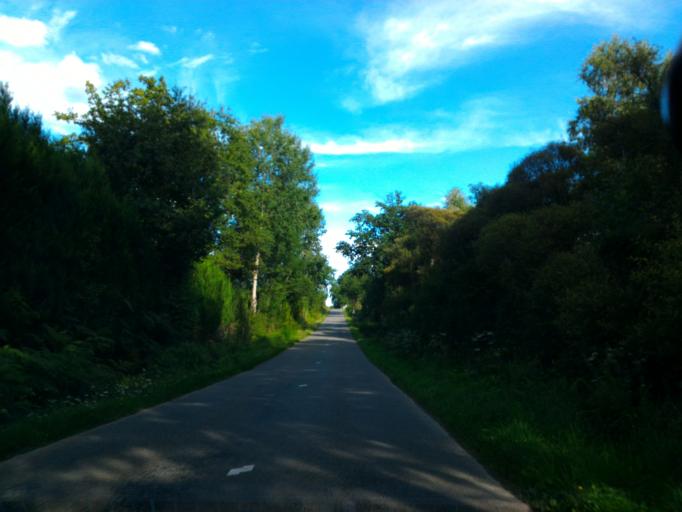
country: FR
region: Poitou-Charentes
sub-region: Departement de la Charente
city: Brigueuil
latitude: 45.9904
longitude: 0.8837
